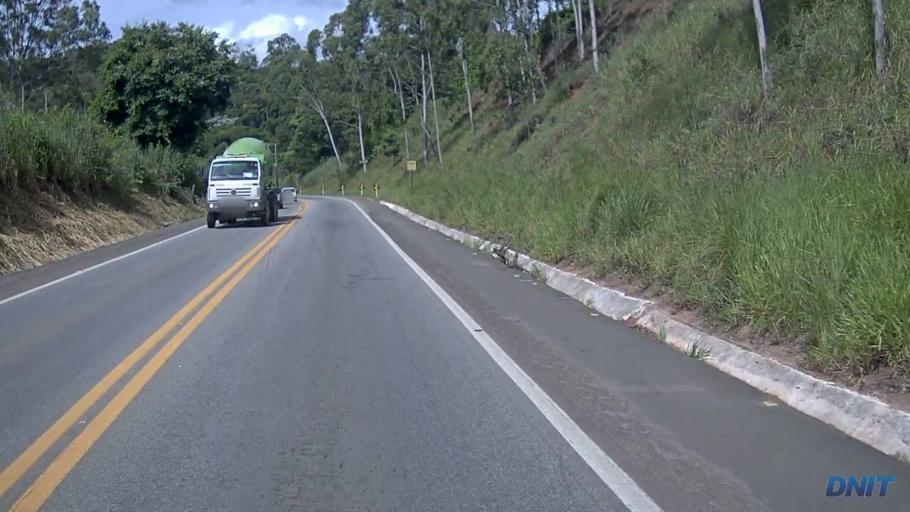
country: BR
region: Minas Gerais
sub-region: Ipatinga
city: Ipatinga
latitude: -19.4247
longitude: -42.4977
